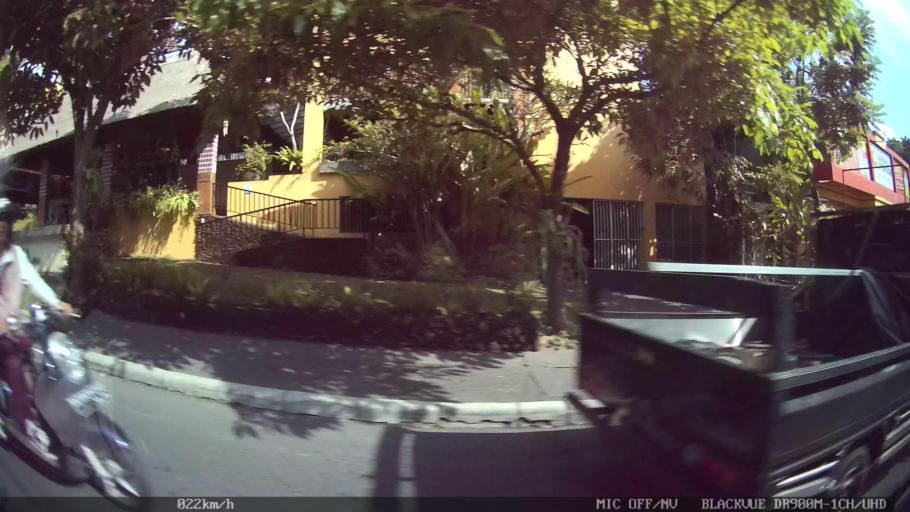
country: ID
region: Bali
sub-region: Kabupaten Gianyar
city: Ubud
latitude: -8.5240
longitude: 115.2668
